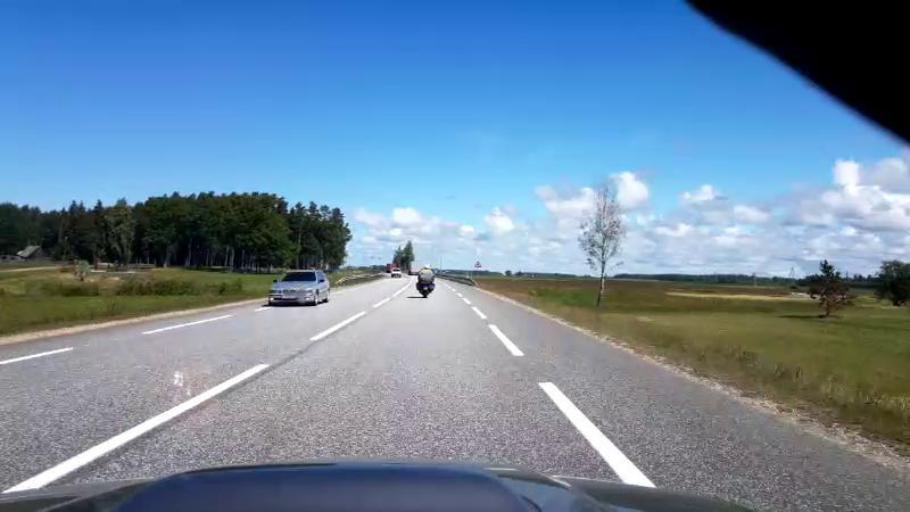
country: LV
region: Saulkrastu
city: Saulkrasti
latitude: 57.4073
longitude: 24.4319
